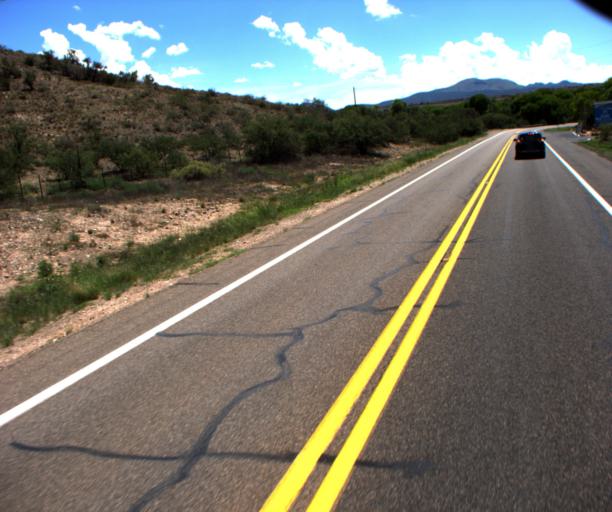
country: US
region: Arizona
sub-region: Yavapai County
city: Camp Verde
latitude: 34.5222
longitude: -111.7759
